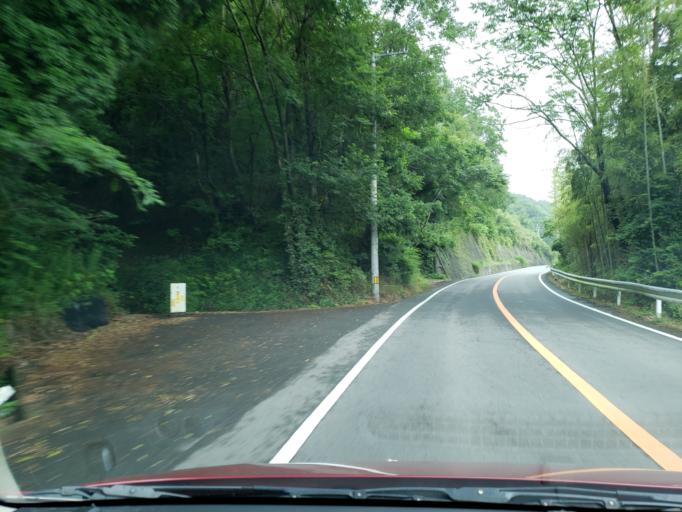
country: JP
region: Tokushima
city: Kamojimacho-jogejima
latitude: 34.1107
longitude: 134.2908
